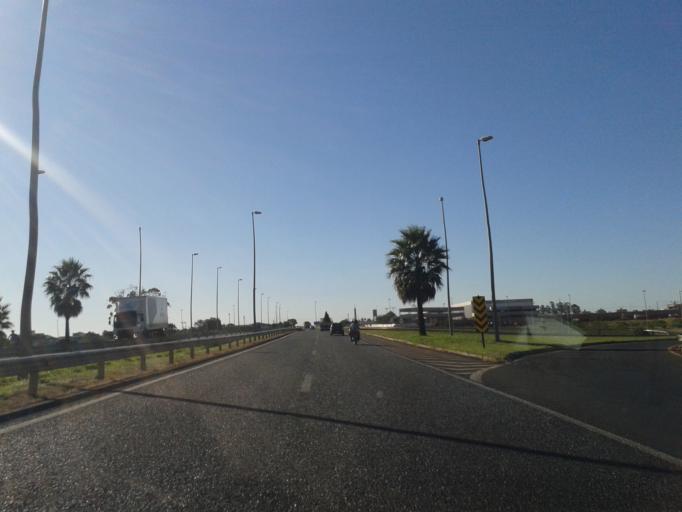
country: BR
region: Minas Gerais
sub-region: Uberlandia
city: Uberlandia
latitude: -18.9403
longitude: -48.2191
